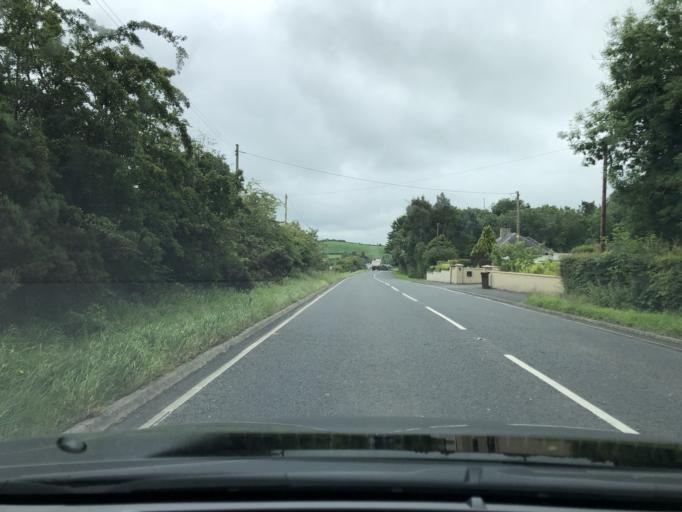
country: GB
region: Northern Ireland
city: Ballynahinch
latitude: 54.3872
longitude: -5.8810
